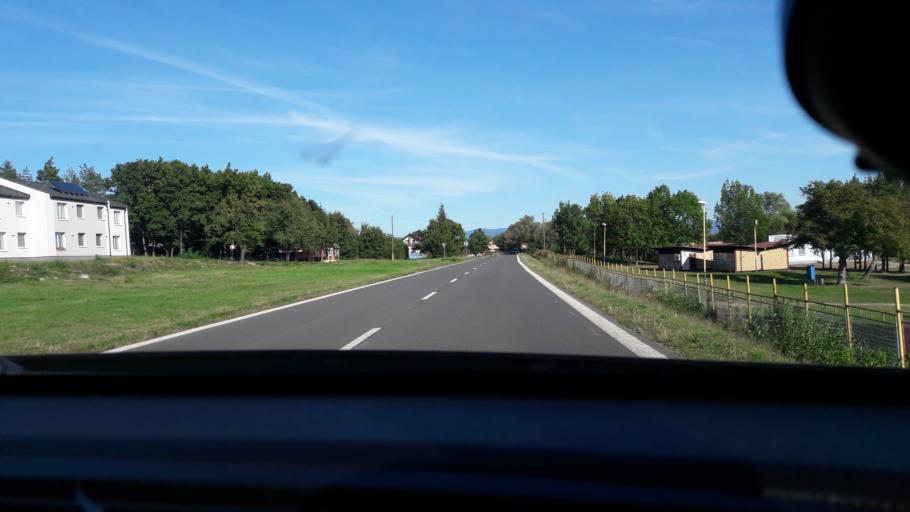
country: SK
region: Kosicky
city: Vinne
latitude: 48.8100
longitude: 22.0213
